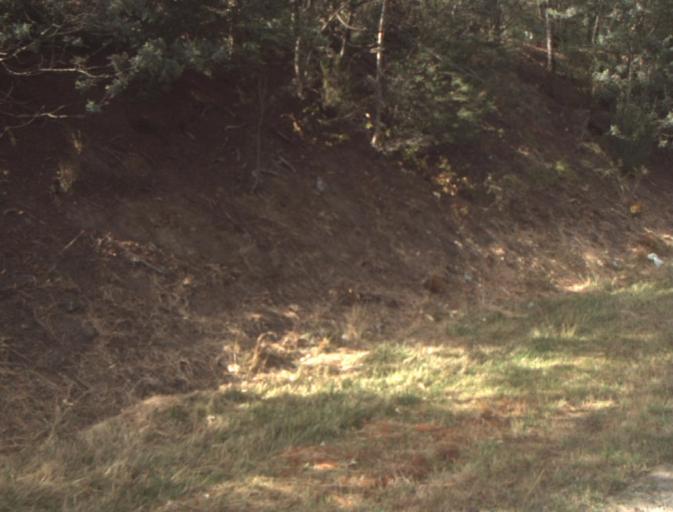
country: AU
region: Tasmania
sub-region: Launceston
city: Mayfield
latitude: -41.2934
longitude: 147.2151
